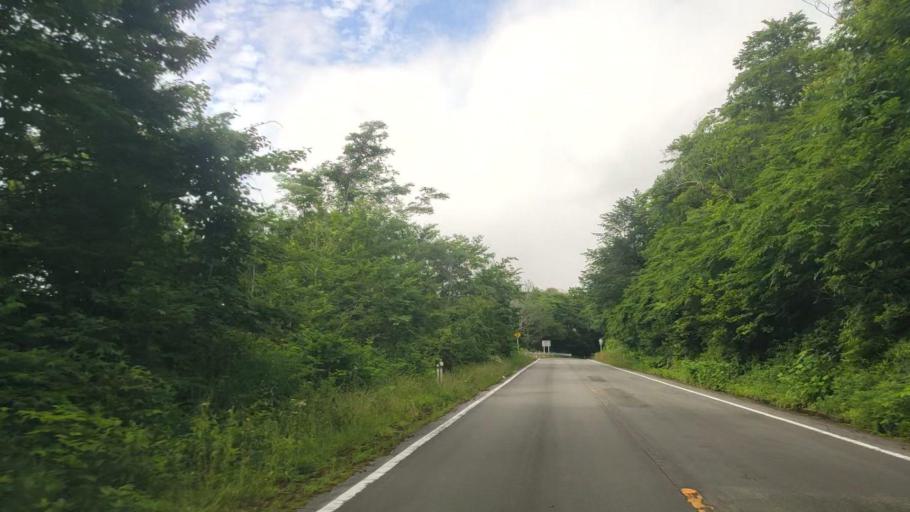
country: JP
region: Tottori
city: Kurayoshi
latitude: 35.3257
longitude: 133.5895
